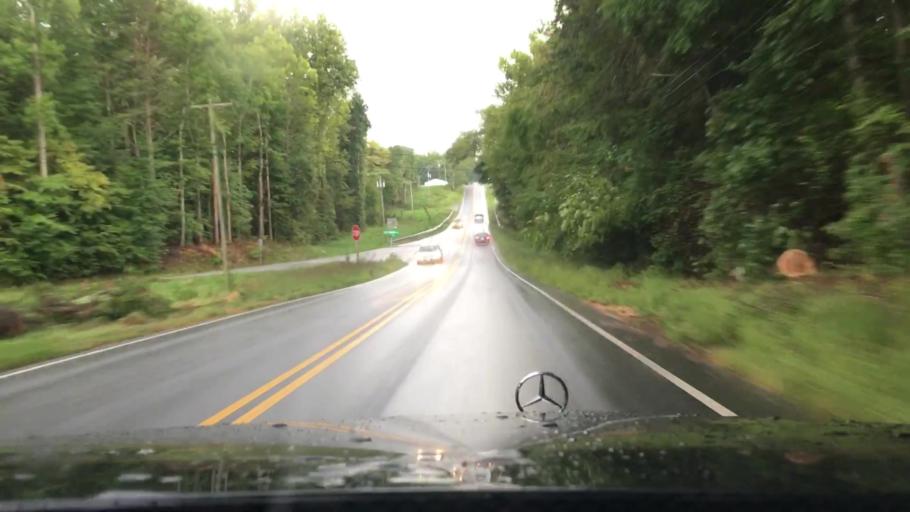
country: US
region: Virginia
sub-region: Amherst County
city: Amherst
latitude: 37.7215
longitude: -79.0162
